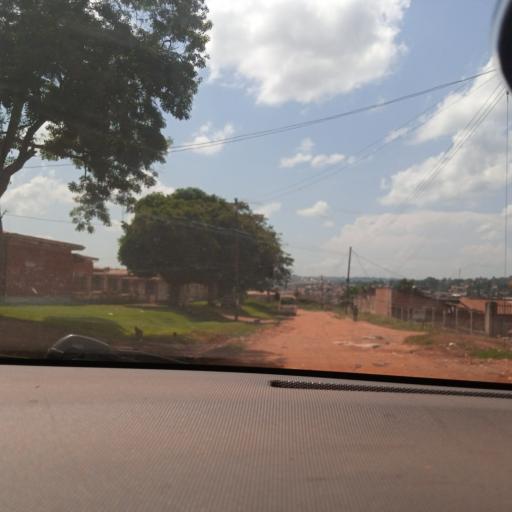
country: UG
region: Central Region
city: Masaka
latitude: -0.3314
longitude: 31.7436
